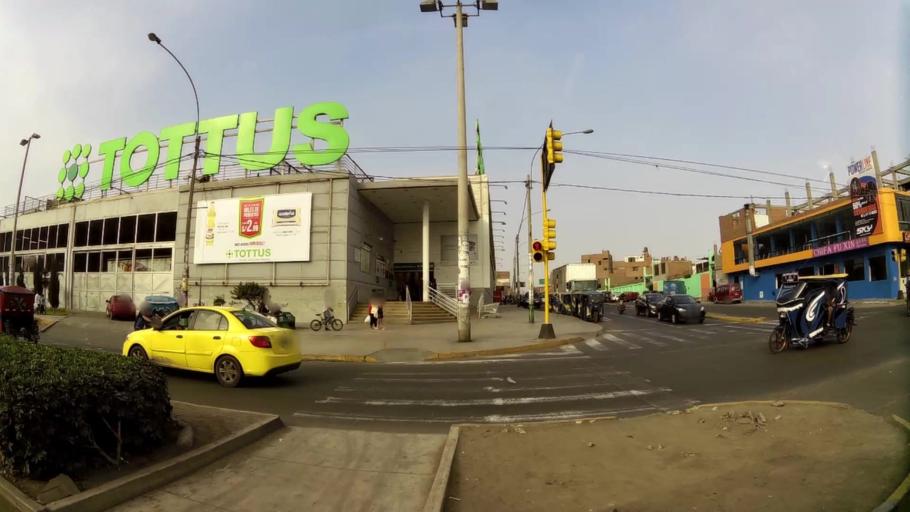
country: PE
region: Callao
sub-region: Callao
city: Callao
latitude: -12.0279
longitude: -77.0945
